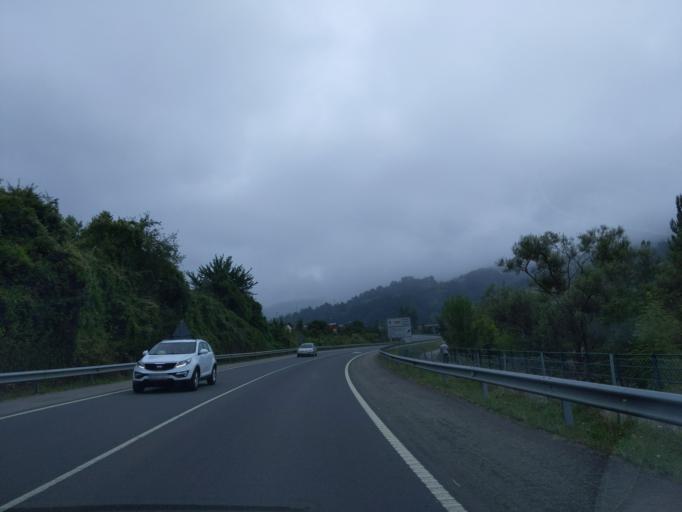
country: ES
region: Asturias
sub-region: Province of Asturias
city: Pola de Laviana
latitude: 43.2452
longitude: -5.5683
